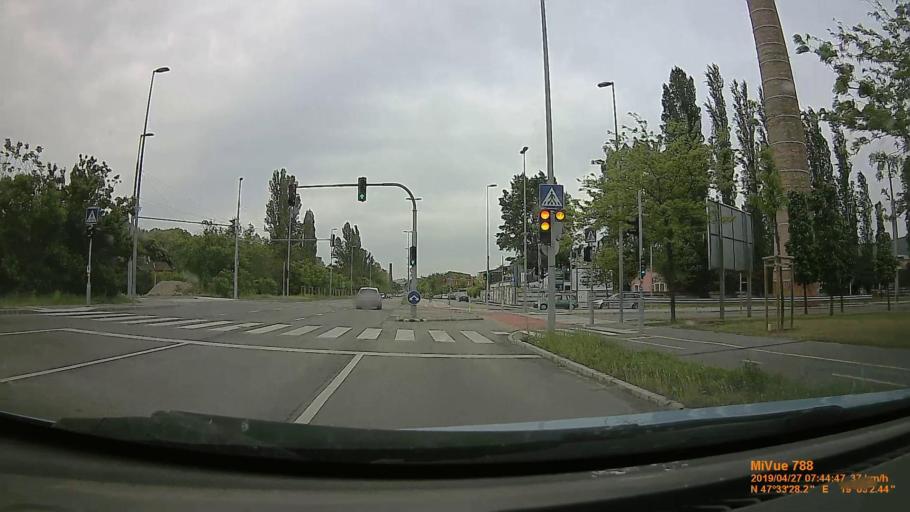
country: HU
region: Budapest
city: Budapest III. keruelet
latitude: 47.5578
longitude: 19.0505
